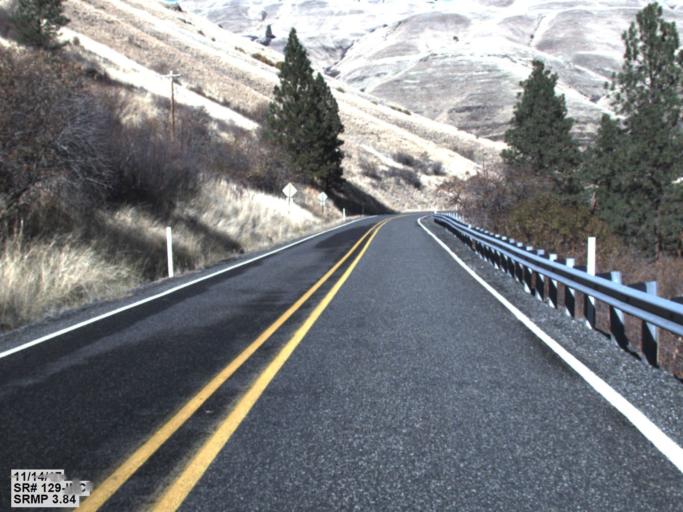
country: US
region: Washington
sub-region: Asotin County
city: Asotin
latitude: 46.0347
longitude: -117.2549
